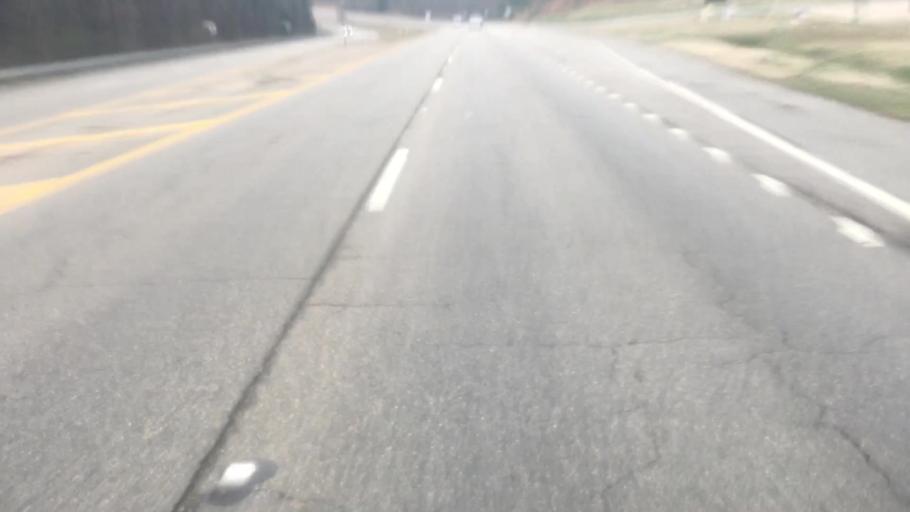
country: US
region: Alabama
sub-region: Walker County
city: Sumiton
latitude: 33.7510
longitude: -87.0588
